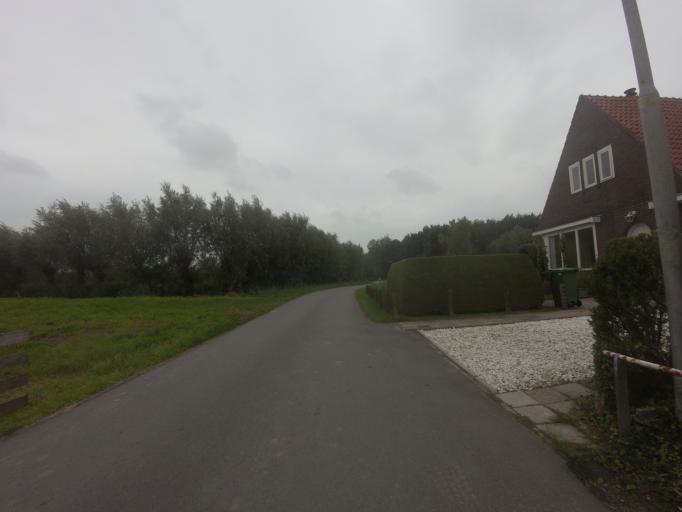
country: NL
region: Friesland
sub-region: Gemeente Leeuwarden
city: Bilgaard
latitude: 53.2232
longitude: 5.7903
